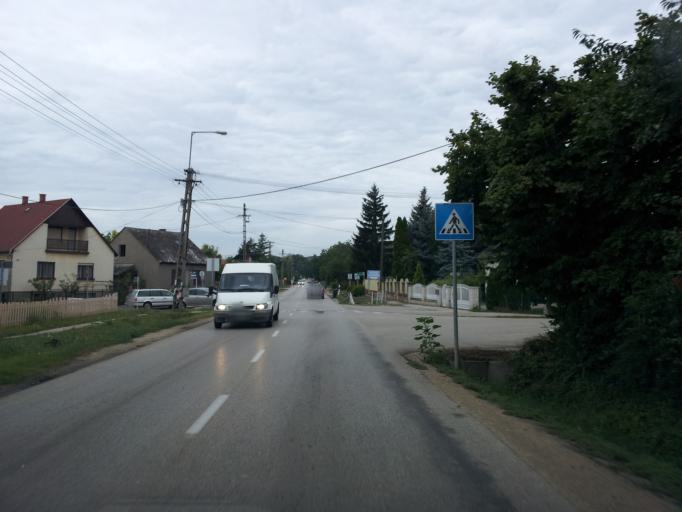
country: HU
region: Fejer
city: Velence
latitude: 47.2407
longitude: 18.6531
